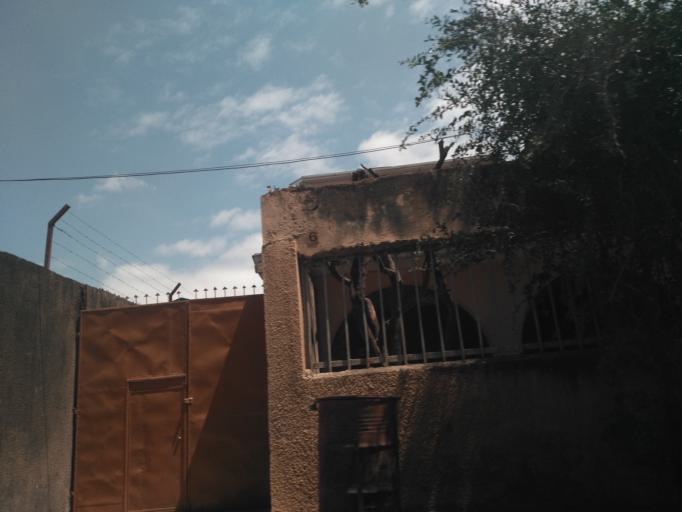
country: TZ
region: Arusha
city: Arusha
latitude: -3.3669
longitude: 36.6871
